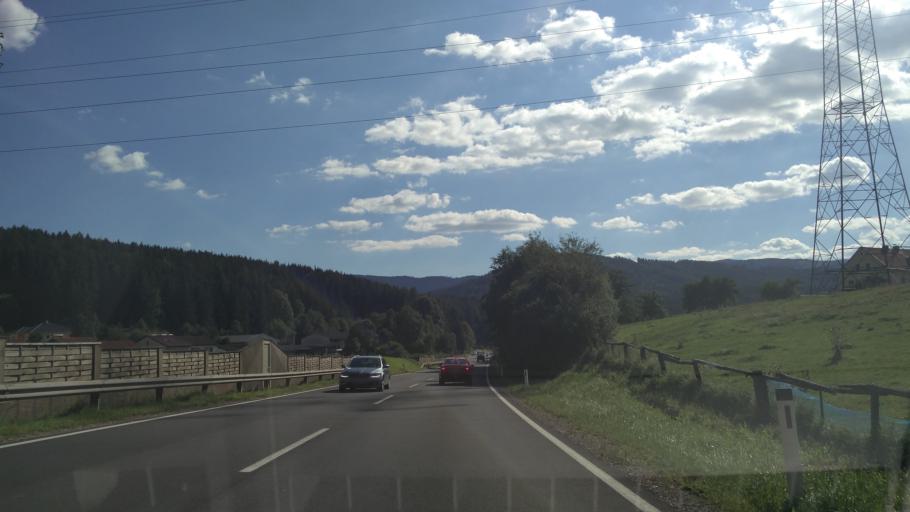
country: AT
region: Styria
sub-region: Politischer Bezirk Leoben
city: Trofaiach
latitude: 47.4070
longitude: 14.9990
